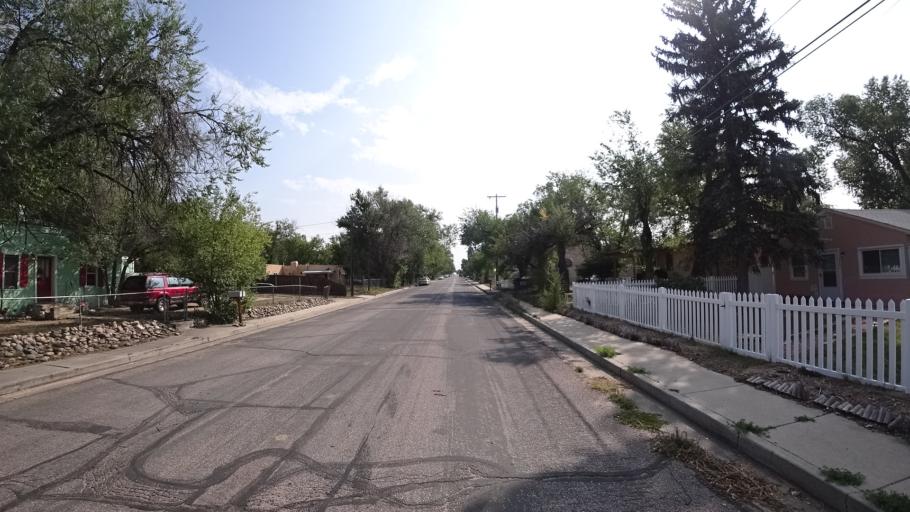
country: US
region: Colorado
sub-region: El Paso County
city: Colorado Springs
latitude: 38.8434
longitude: -104.7826
